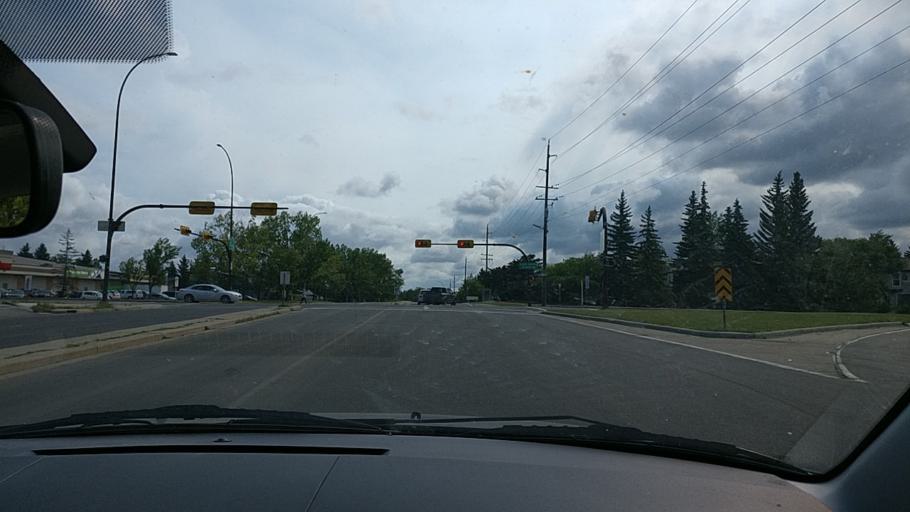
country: CA
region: Alberta
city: Calgary
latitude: 51.1035
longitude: -114.1901
